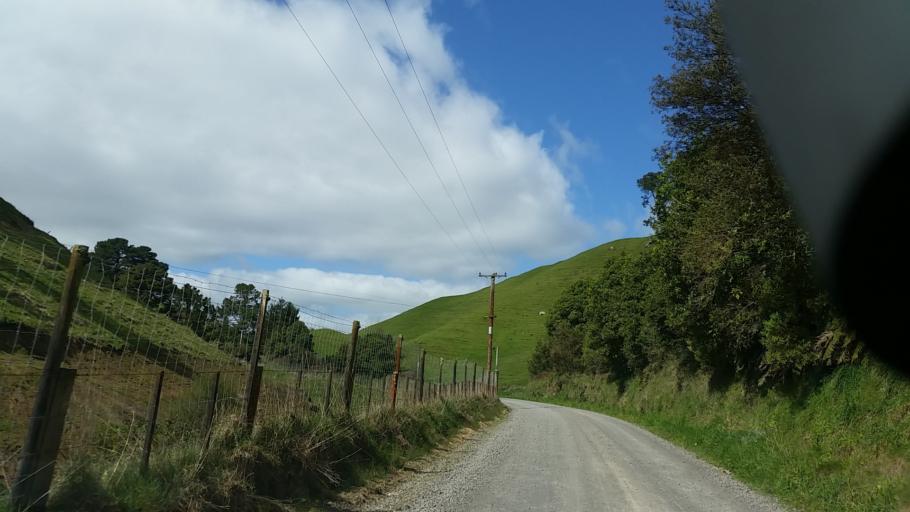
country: NZ
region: Bay of Plenty
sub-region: Rotorua District
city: Rotorua
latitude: -38.3997
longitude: 176.1792
